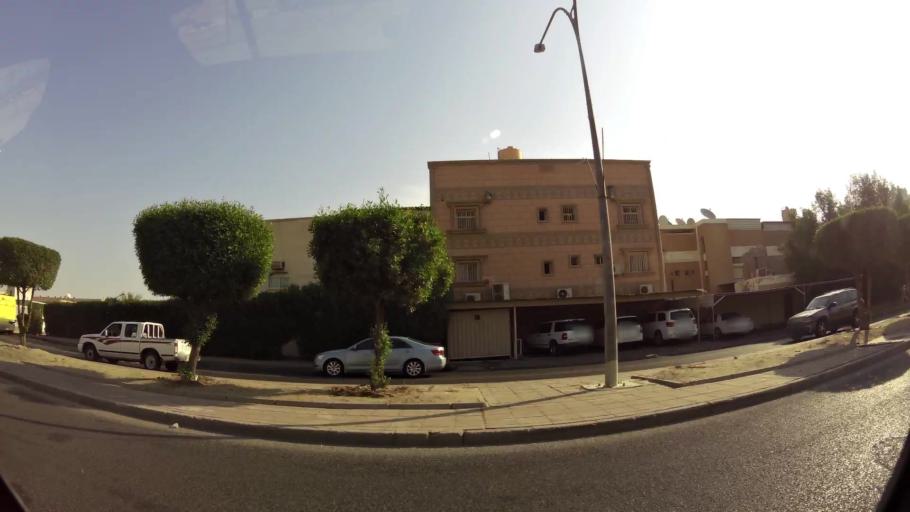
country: KW
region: Al Ahmadi
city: Ar Riqqah
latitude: 29.1622
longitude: 48.0674
